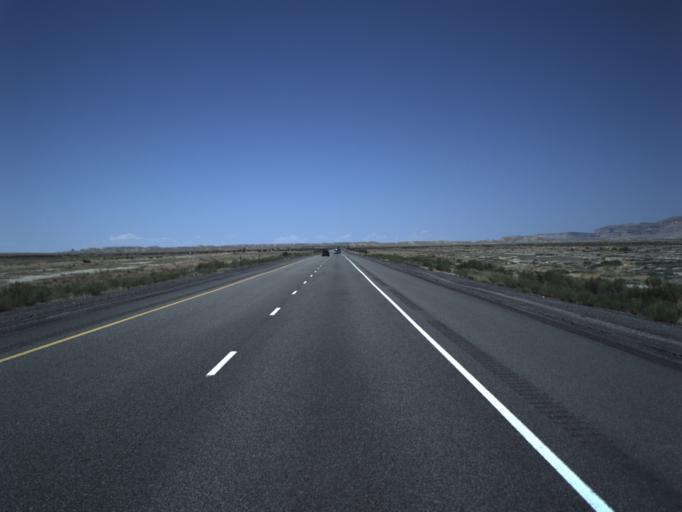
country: US
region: Utah
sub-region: Grand County
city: Moab
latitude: 38.9428
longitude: -109.5752
